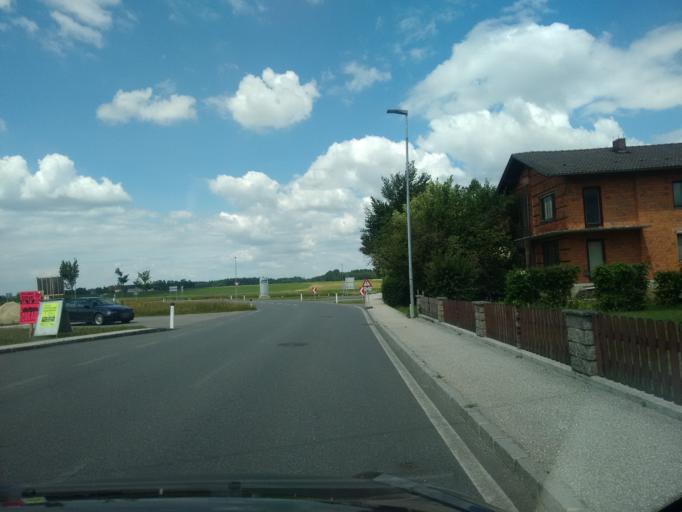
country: AT
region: Upper Austria
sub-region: Politischer Bezirk Steyr-Land
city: Sierning
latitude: 48.0465
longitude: 14.3009
